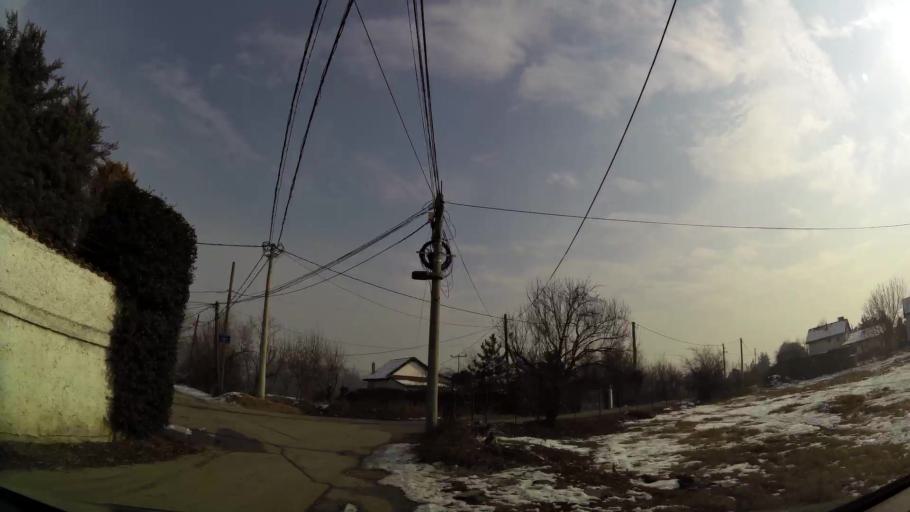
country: MK
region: Suto Orizari
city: Suto Orizare
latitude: 42.0156
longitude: 21.3871
